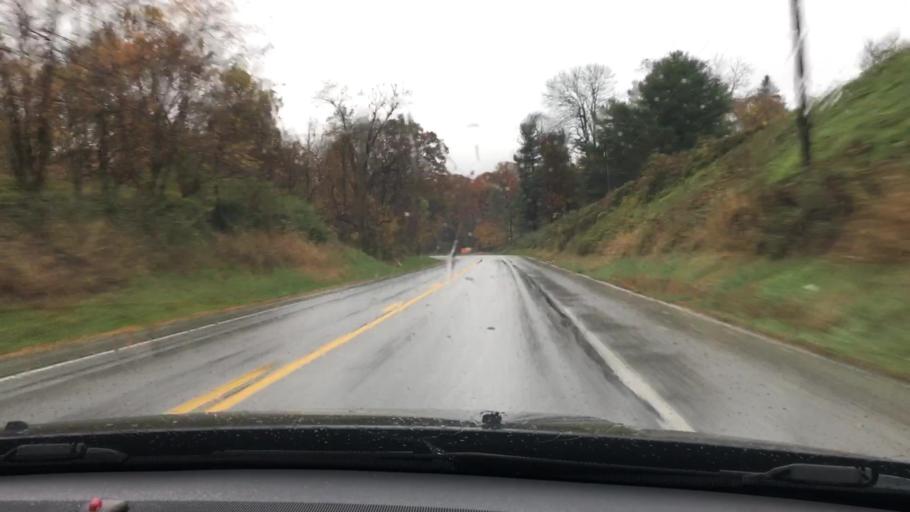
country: US
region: Pennsylvania
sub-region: York County
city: Susquehanna Trails
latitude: 39.8365
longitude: -76.3086
